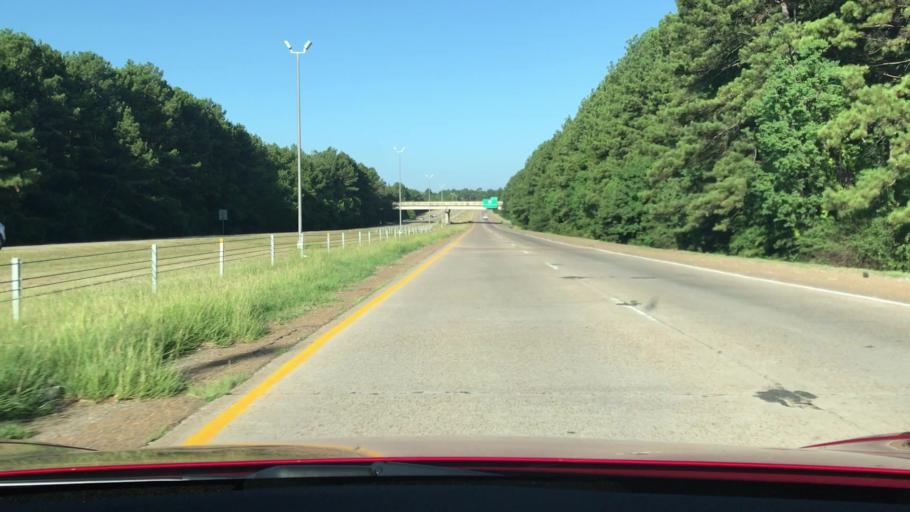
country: US
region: Louisiana
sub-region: Bossier Parish
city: Bossier City
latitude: 32.4195
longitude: -93.7773
